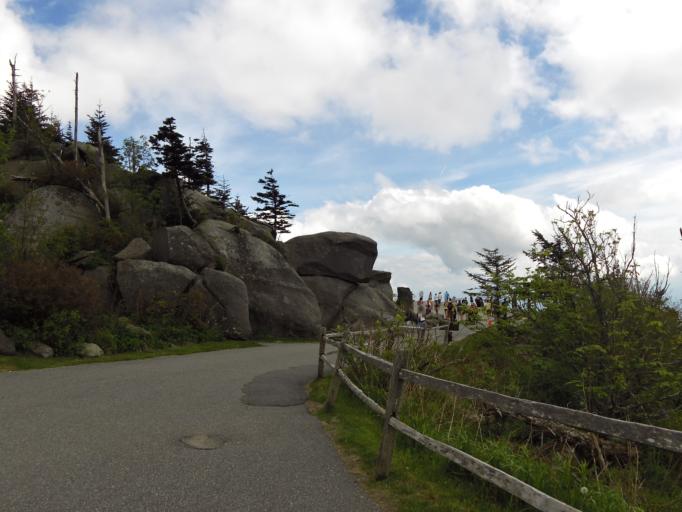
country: US
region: North Carolina
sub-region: Swain County
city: Bryson City
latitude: 35.5573
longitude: -83.4963
